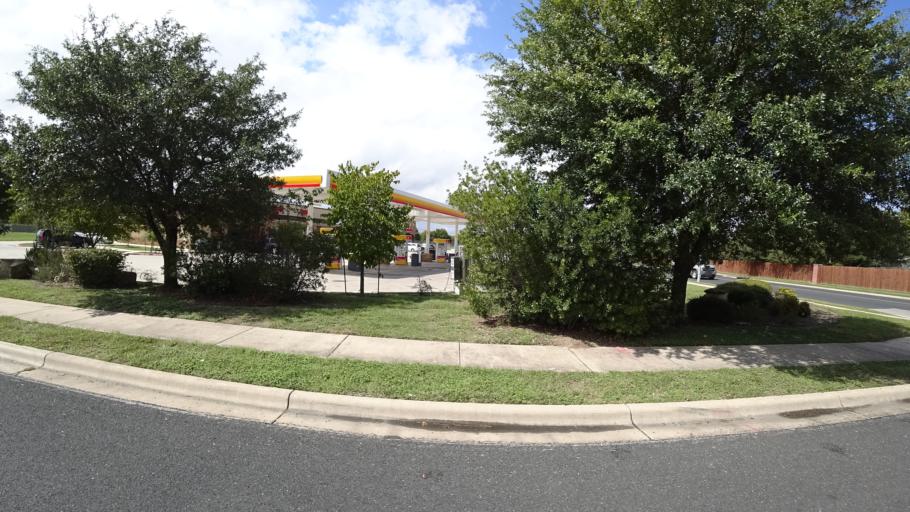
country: US
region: Texas
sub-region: Travis County
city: Onion Creek
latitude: 30.1576
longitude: -97.7436
